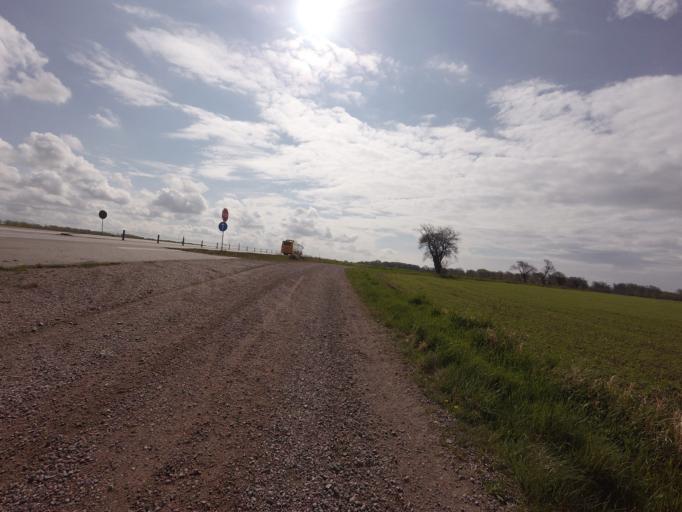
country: DK
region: Capital Region
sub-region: Helsingor Kommune
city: Helsingor
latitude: 56.1176
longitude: 12.6291
